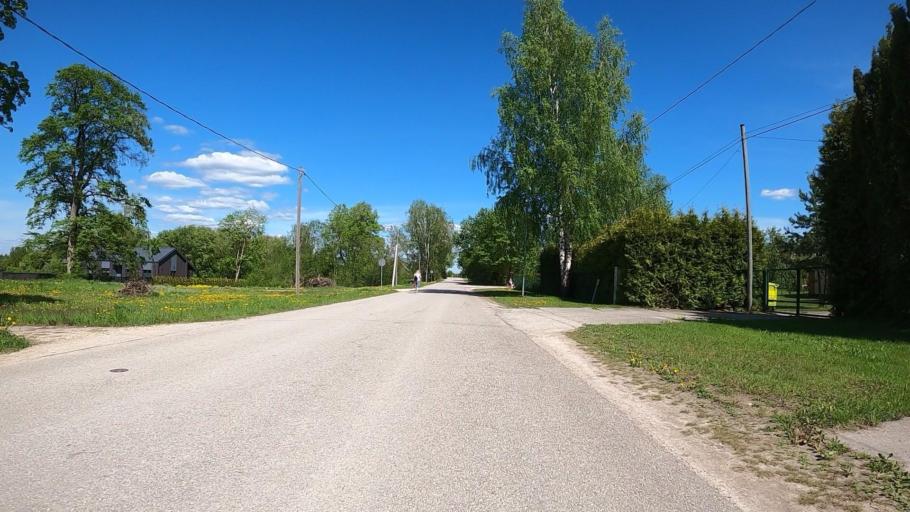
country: LV
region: Kekava
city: Kekava
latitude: 56.8252
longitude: 24.2511
